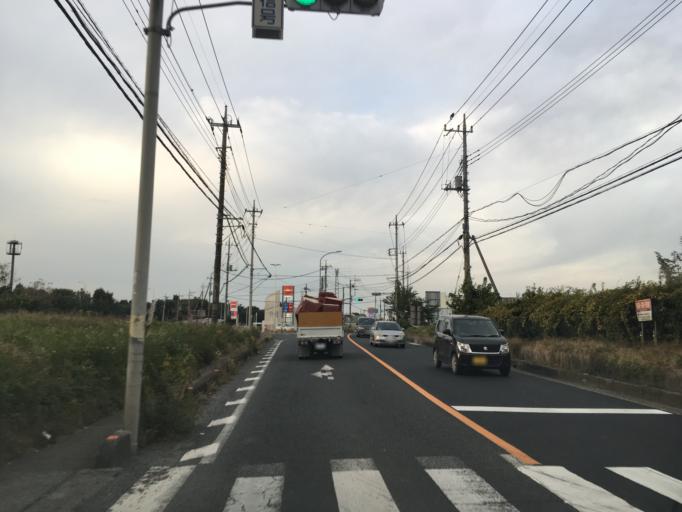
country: JP
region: Saitama
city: Sayama
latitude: 35.8611
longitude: 139.3795
